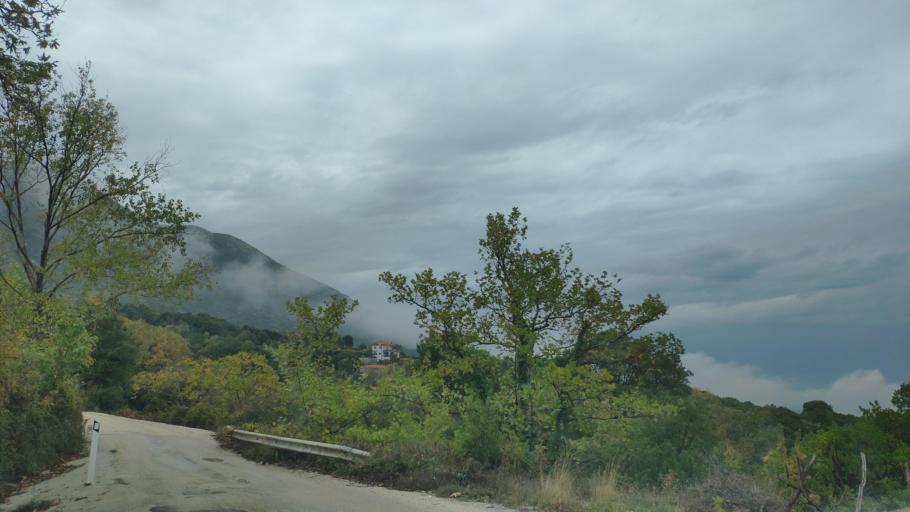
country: GR
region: Epirus
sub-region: Nomos Thesprotias
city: Paramythia
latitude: 39.4596
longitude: 20.6783
